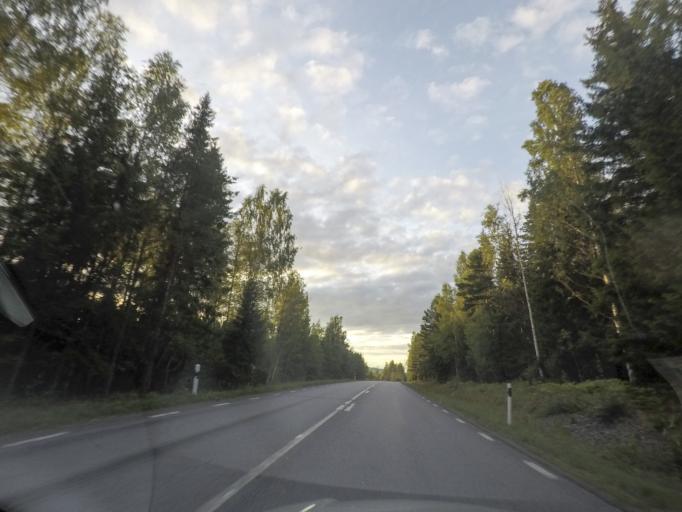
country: SE
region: OErebro
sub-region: Hallefors Kommun
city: Haellefors
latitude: 59.7166
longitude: 14.5282
